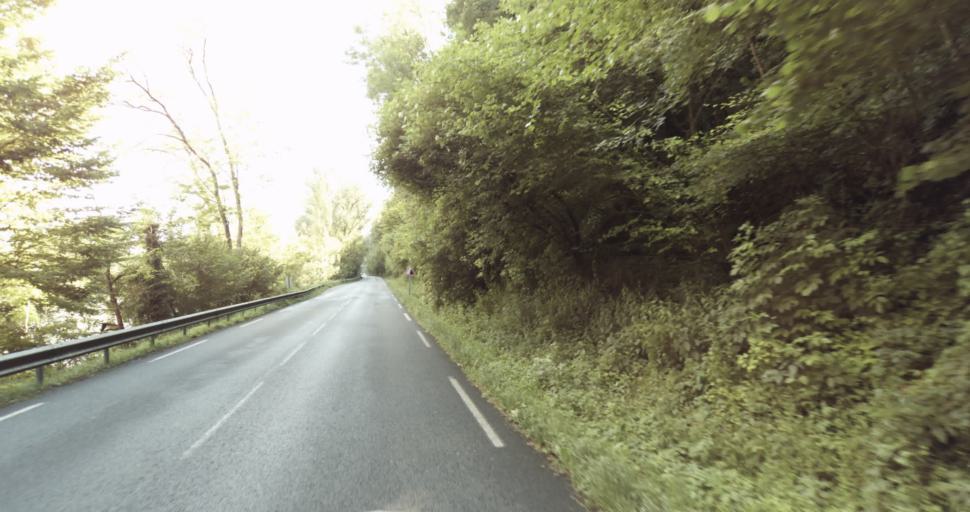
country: FR
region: Aquitaine
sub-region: Departement de la Dordogne
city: Lalinde
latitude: 44.8481
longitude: 0.7986
